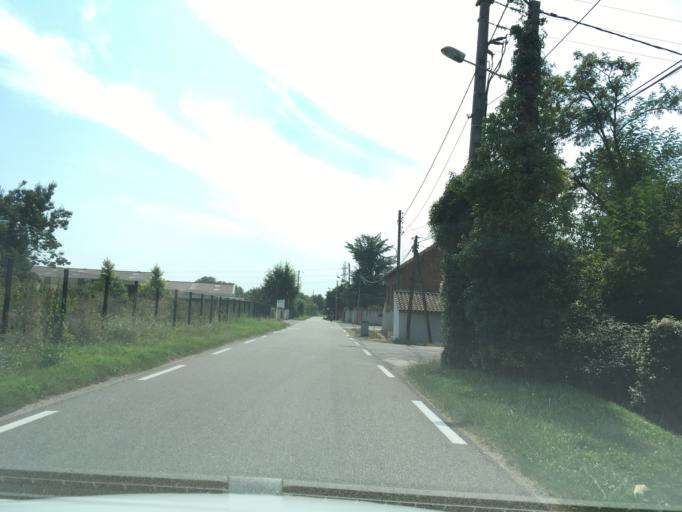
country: FR
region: Midi-Pyrenees
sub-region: Departement du Tarn-et-Garonne
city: Montauban
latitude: 44.0128
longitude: 1.3384
